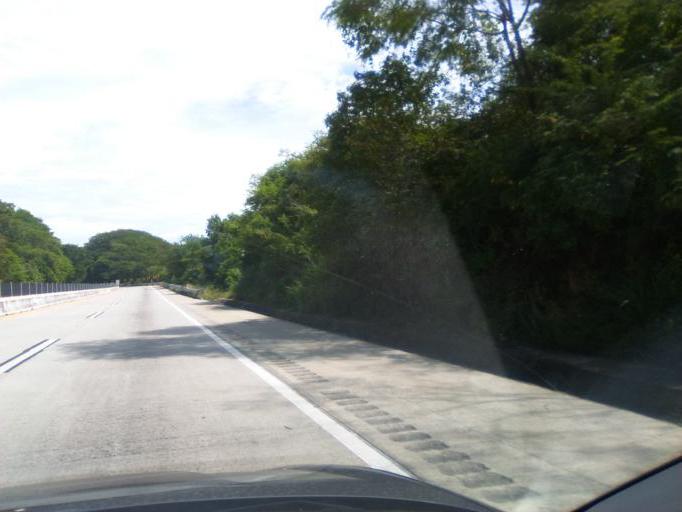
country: MX
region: Guerrero
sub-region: Acapulco de Juarez
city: Pueblo Madero (El Playon)
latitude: 17.0745
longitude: -99.6118
